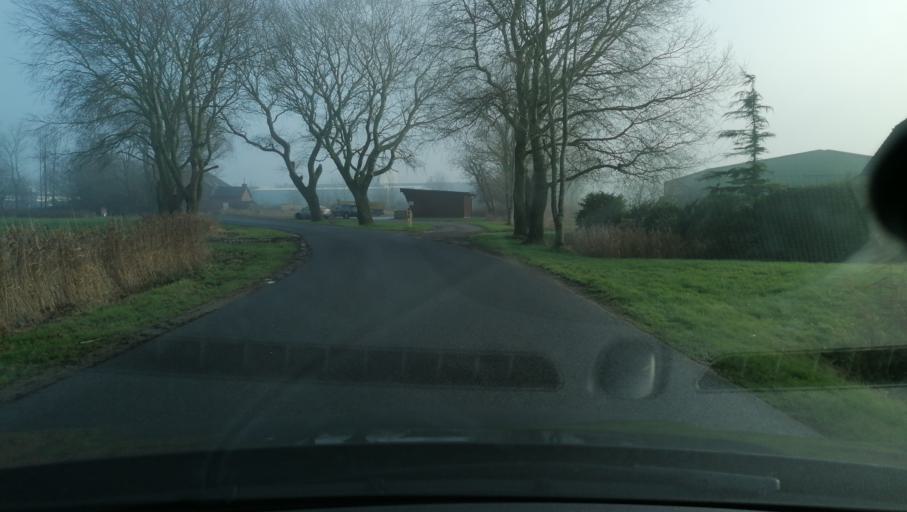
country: DE
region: Schleswig-Holstein
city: Meldorf
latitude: 54.0976
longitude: 9.0586
